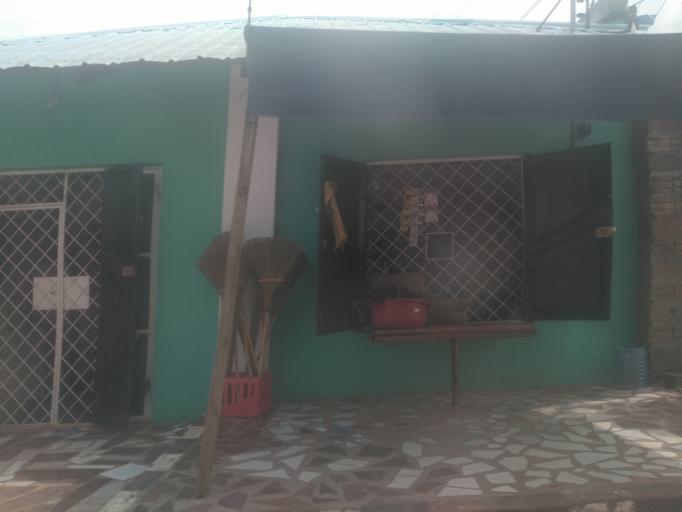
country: TZ
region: Zanzibar Urban/West
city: Zanzibar
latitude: -6.2341
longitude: 39.2128
